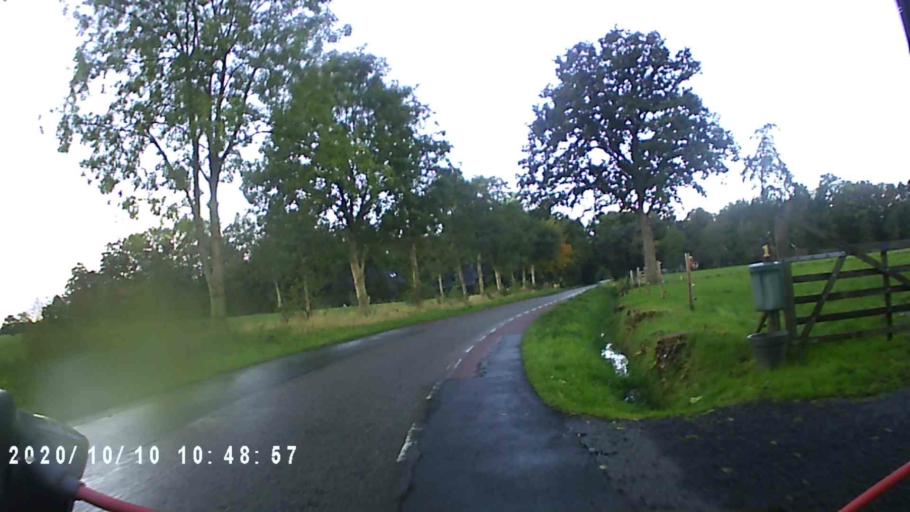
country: NL
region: Groningen
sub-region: Gemeente Grootegast
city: Grootegast
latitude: 53.1626
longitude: 6.2412
